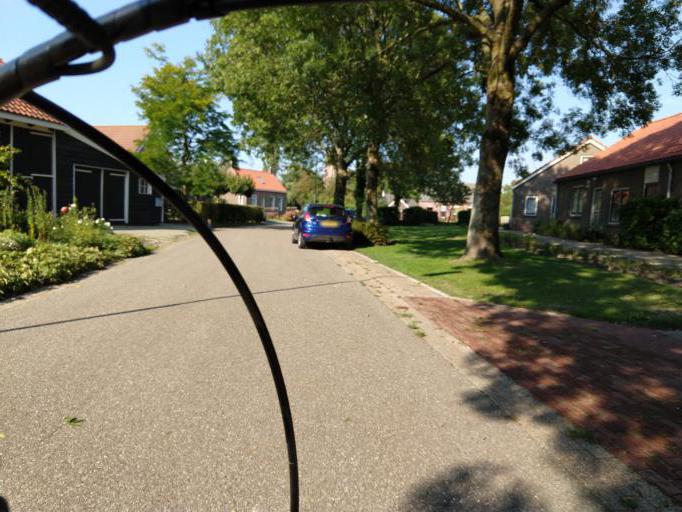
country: NL
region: Zeeland
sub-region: Gemeente Goes
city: Goes
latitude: 51.4691
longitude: 3.8797
